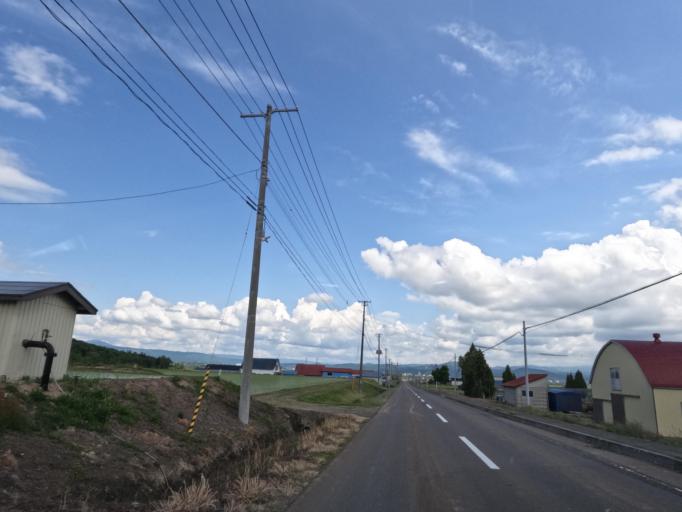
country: JP
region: Hokkaido
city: Takikawa
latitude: 43.5761
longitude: 141.8485
